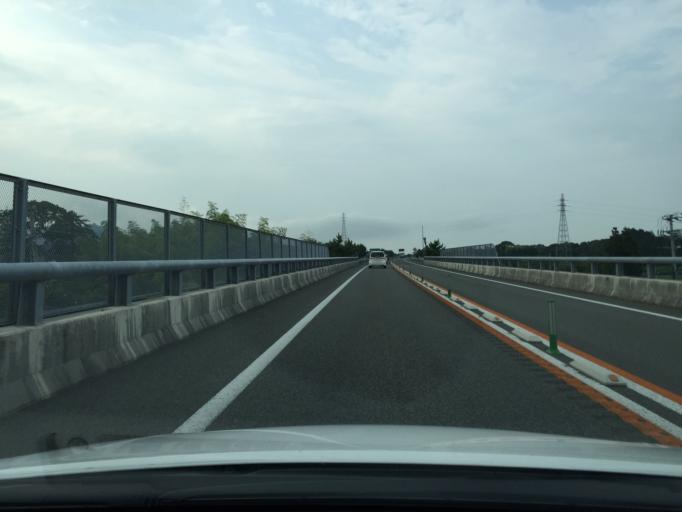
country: JP
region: Fukushima
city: Namie
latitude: 37.3663
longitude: 140.9682
